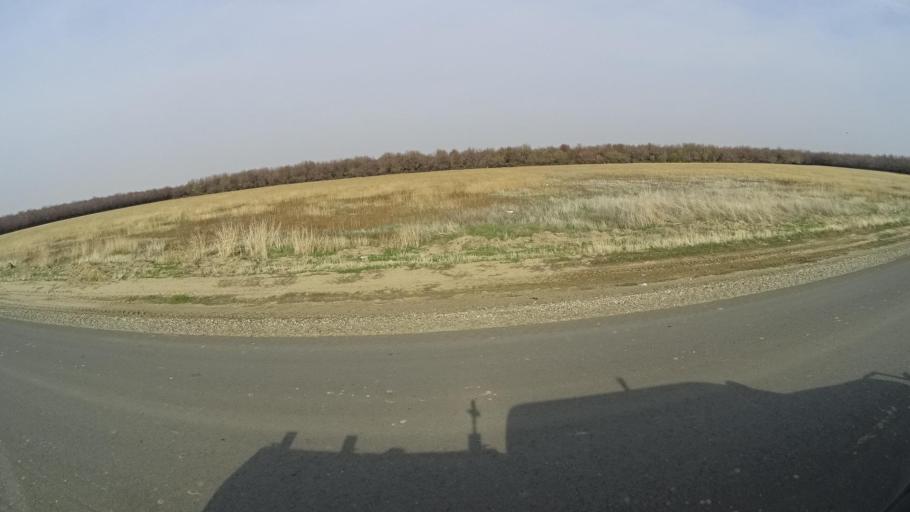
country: US
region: California
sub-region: Kern County
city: Arvin
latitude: 35.0454
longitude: -118.8892
